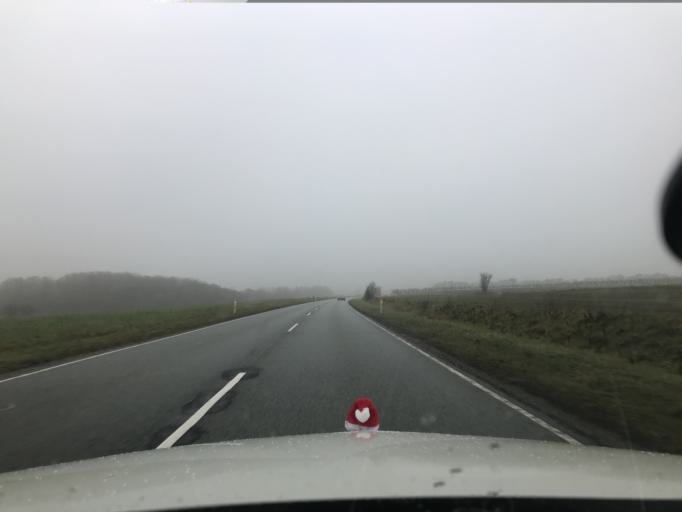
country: DK
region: South Denmark
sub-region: Aabenraa Kommune
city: Aabenraa
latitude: 55.0019
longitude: 9.4112
